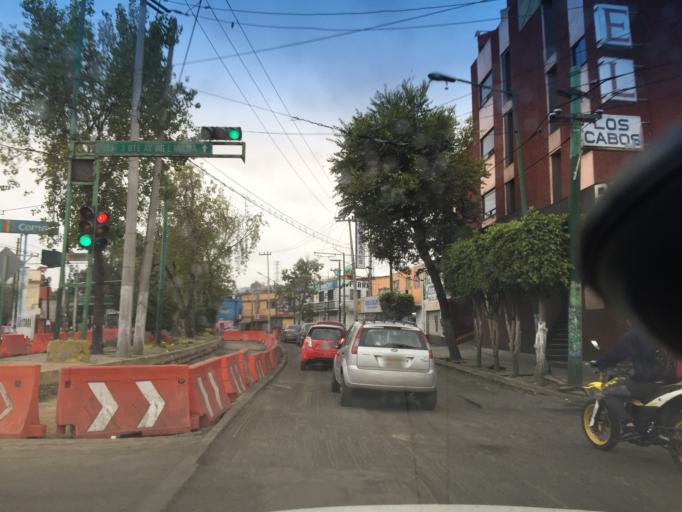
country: MX
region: Mexico City
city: Gustavo A. Madero
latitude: 19.4750
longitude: -99.0887
